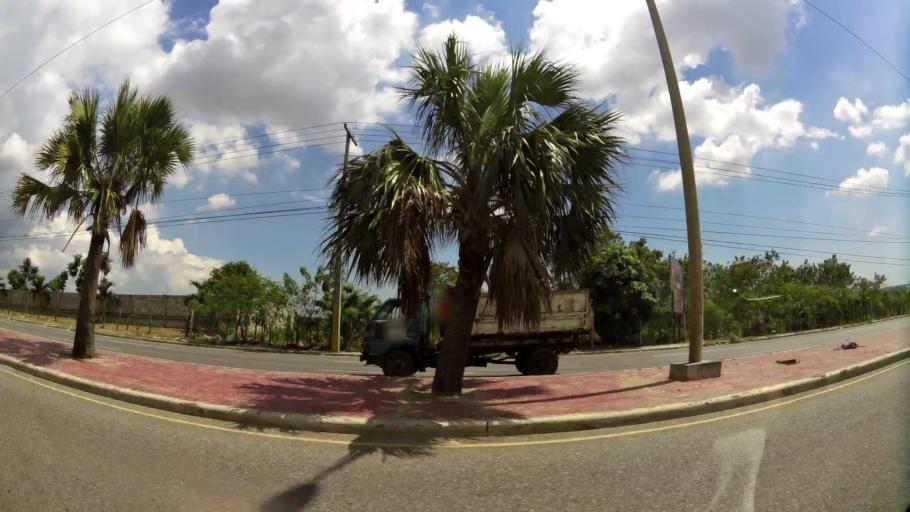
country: DO
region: Nacional
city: La Agustina
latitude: 18.5503
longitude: -69.9480
